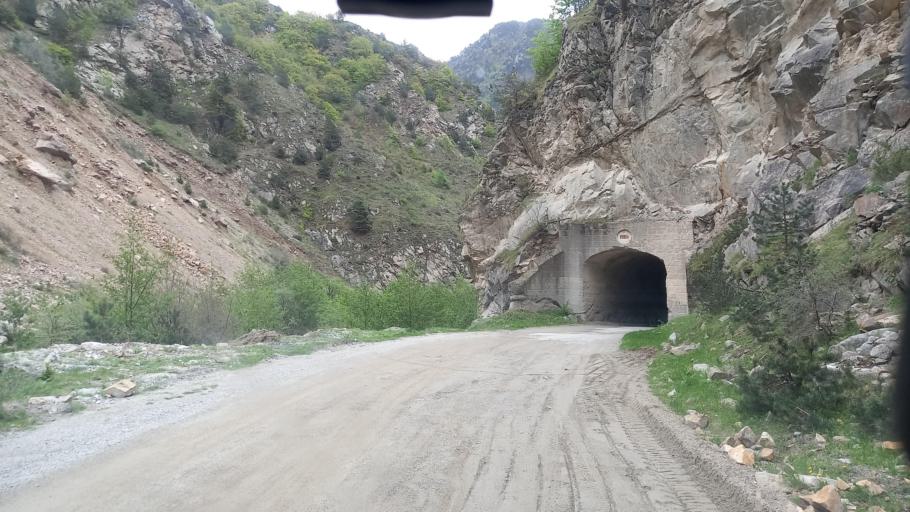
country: RU
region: North Ossetia
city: Mizur
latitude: 42.8417
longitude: 44.0248
